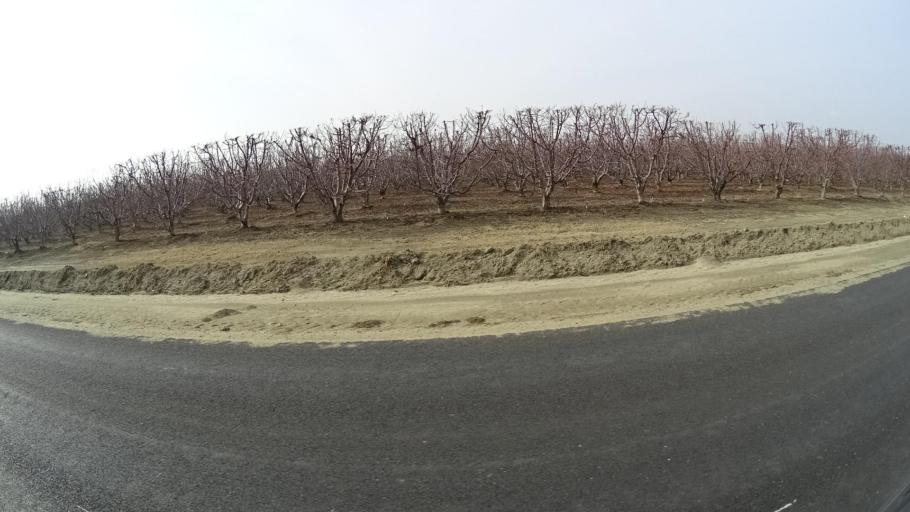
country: US
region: California
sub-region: Kern County
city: Arvin
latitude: 35.1600
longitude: -118.8509
